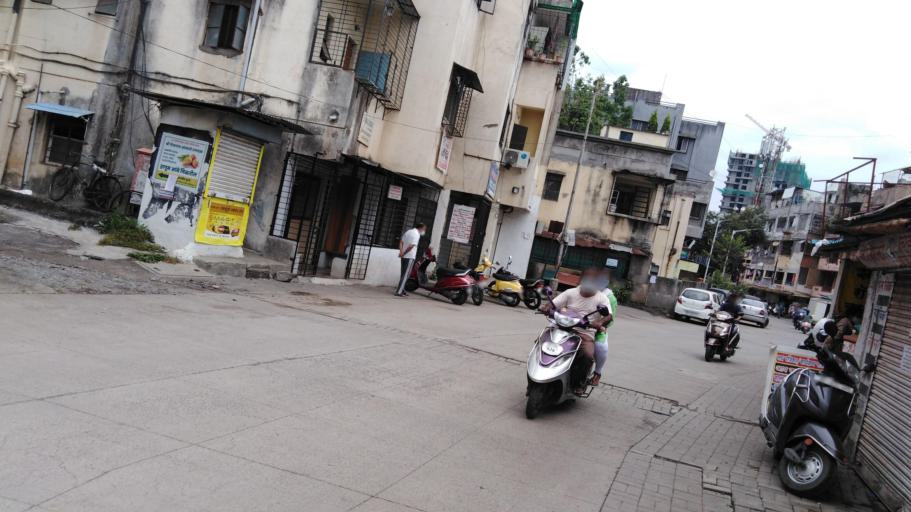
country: IN
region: Maharashtra
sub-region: Pune Division
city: Pune
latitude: 18.4795
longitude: 73.8284
